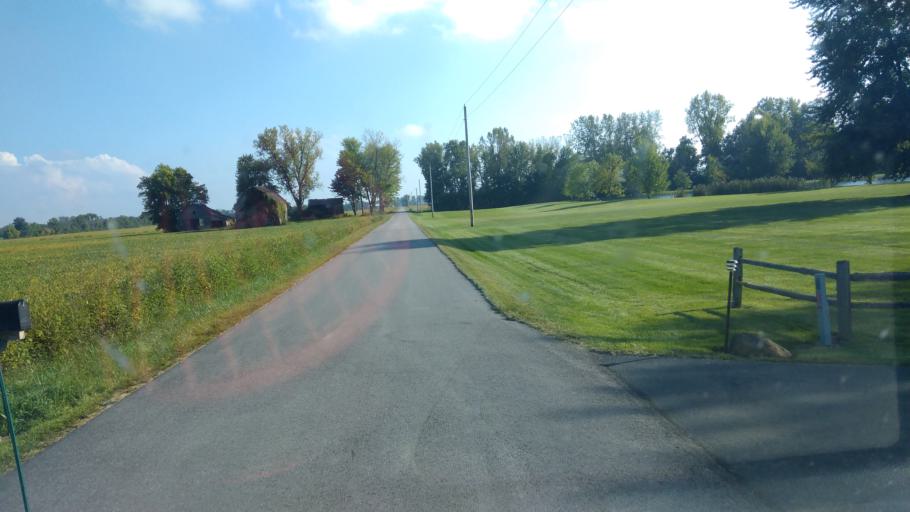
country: US
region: Ohio
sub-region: Hardin County
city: Forest
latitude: 40.7295
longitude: -83.4779
